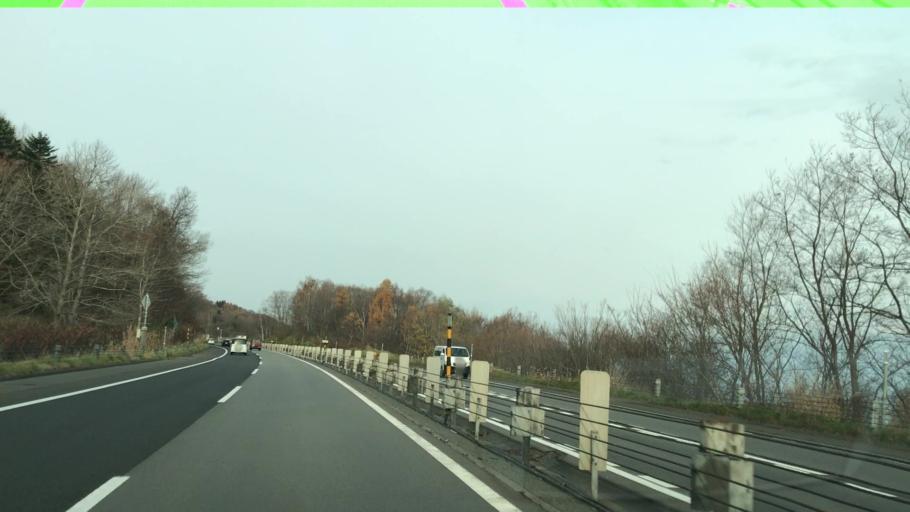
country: JP
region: Hokkaido
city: Otaru
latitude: 43.1440
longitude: 141.1412
